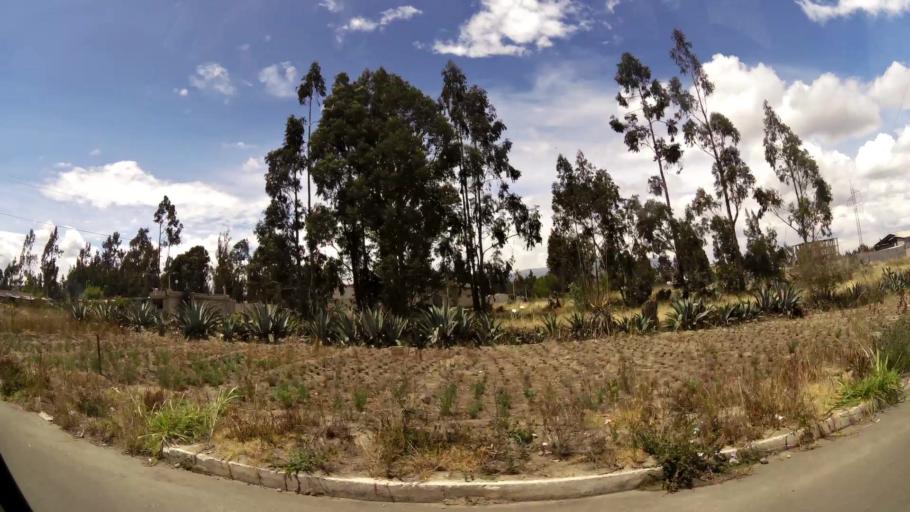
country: EC
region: Tungurahua
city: Ambato
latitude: -1.2810
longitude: -78.5997
